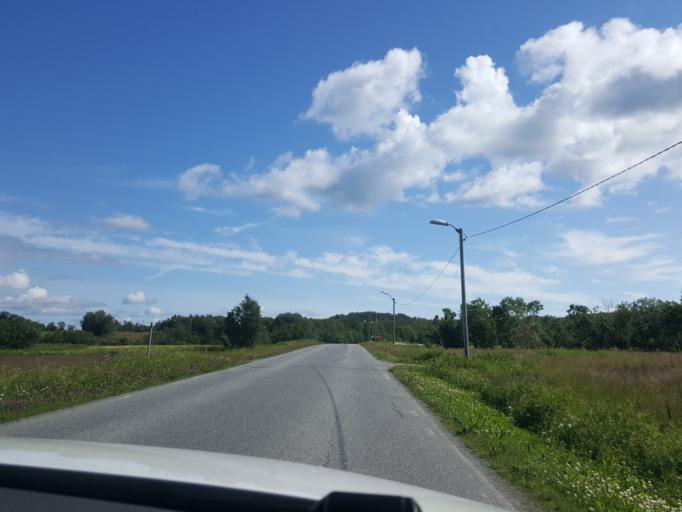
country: NO
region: Nordland
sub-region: Bodo
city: Loding
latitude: 67.2299
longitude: 14.9100
